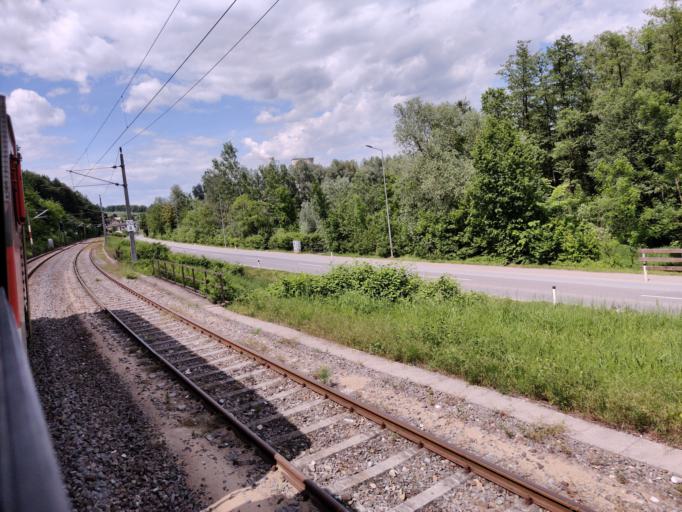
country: AT
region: Styria
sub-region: Politischer Bezirk Leibnitz
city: Retznei
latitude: 46.7308
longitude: 15.5728
